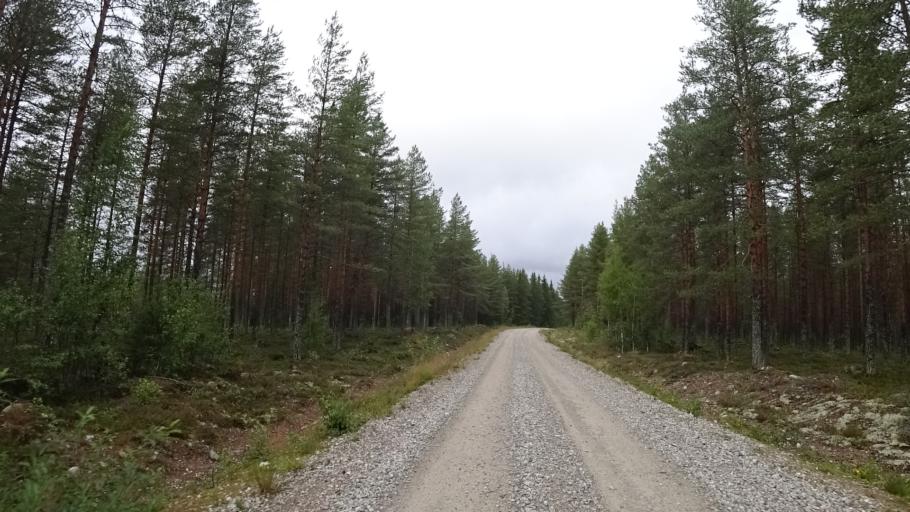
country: FI
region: North Karelia
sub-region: Pielisen Karjala
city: Lieksa
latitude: 63.4741
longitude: 30.2665
